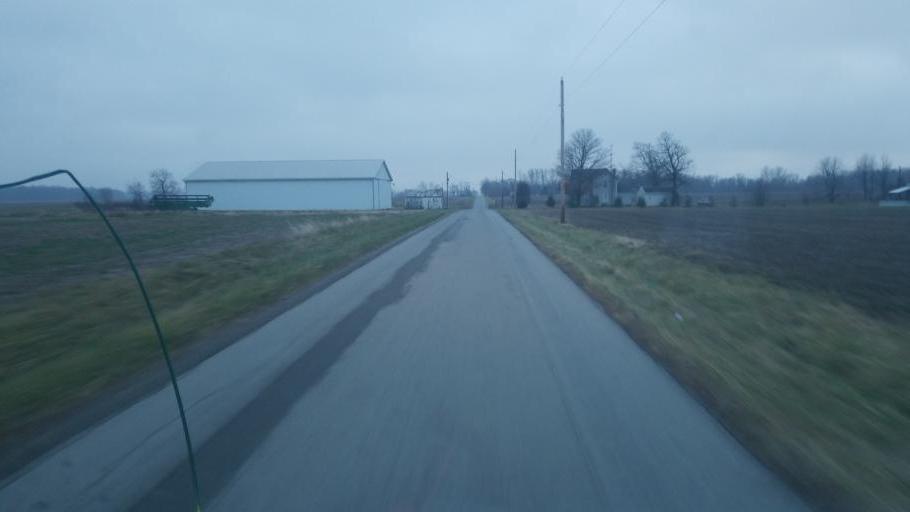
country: US
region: Ohio
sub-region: Seneca County
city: Tiffin
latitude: 40.9700
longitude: -83.1318
